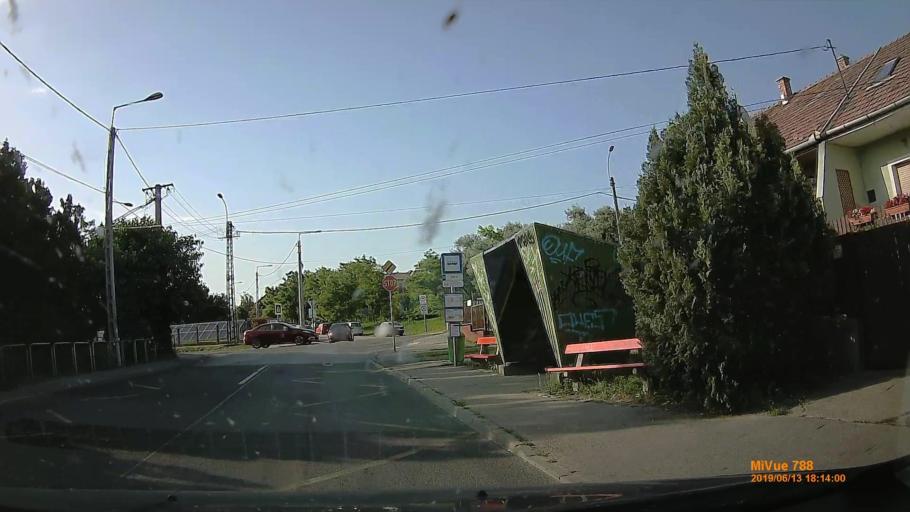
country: HU
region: Pest
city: Ecser
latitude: 47.4640
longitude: 19.3126
